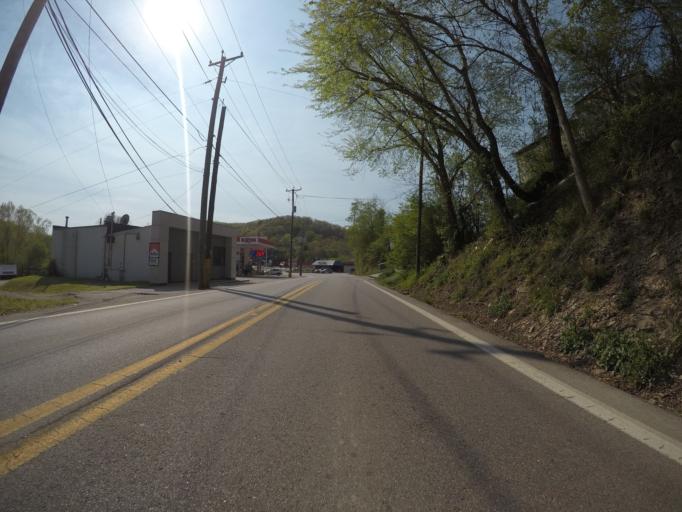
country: US
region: West Virginia
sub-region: Kanawha County
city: Pinch
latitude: 38.4064
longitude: -81.5385
